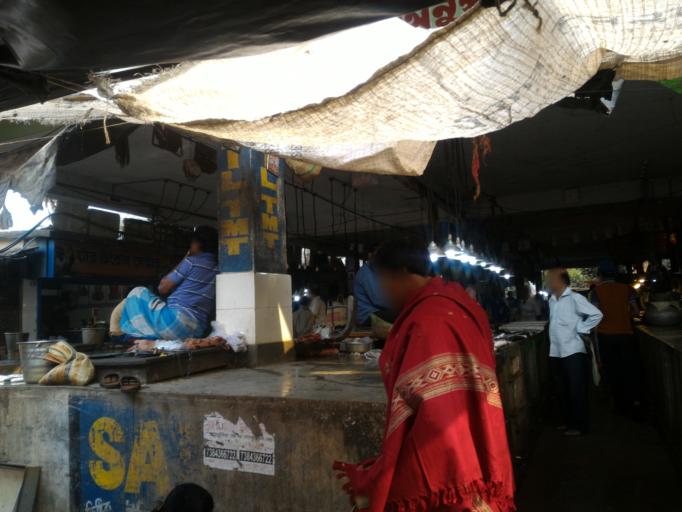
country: IN
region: West Bengal
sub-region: North 24 Parganas
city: Bangaon
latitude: 23.0396
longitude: 88.8274
